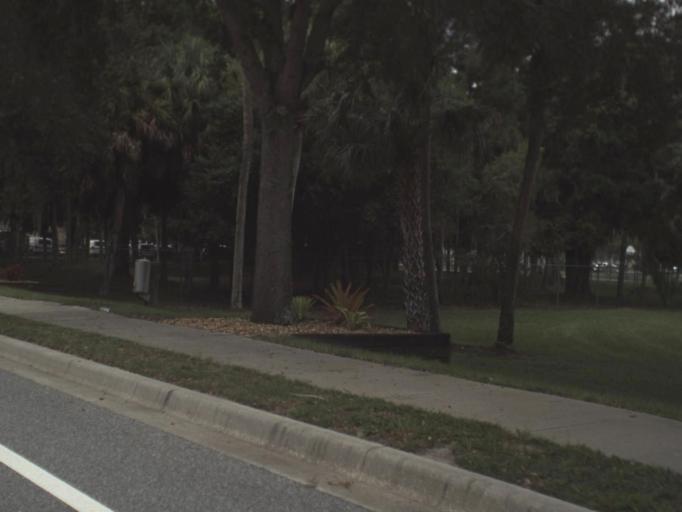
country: US
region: Florida
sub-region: Manatee County
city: Whitfield
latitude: 27.3821
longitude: -82.5536
